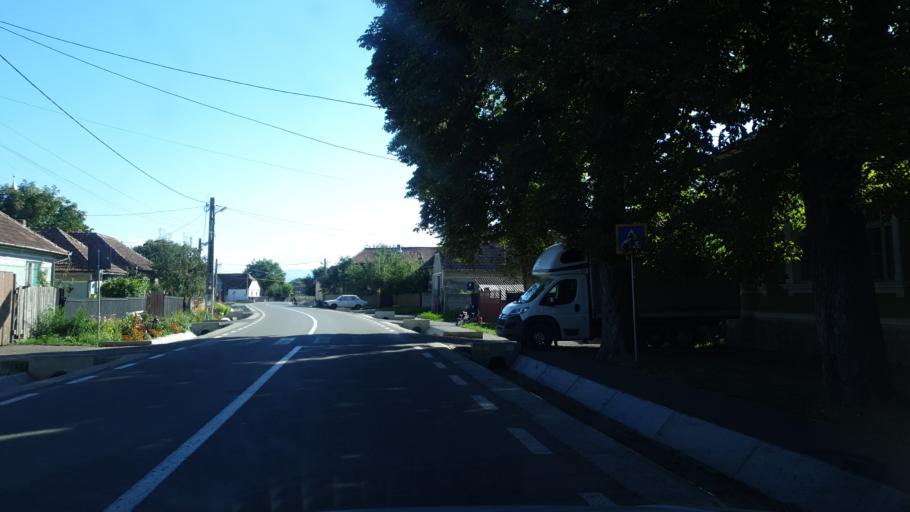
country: RO
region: Covasna
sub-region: Comuna Ilieni
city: Ilieni
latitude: 45.7816
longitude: 25.7559
